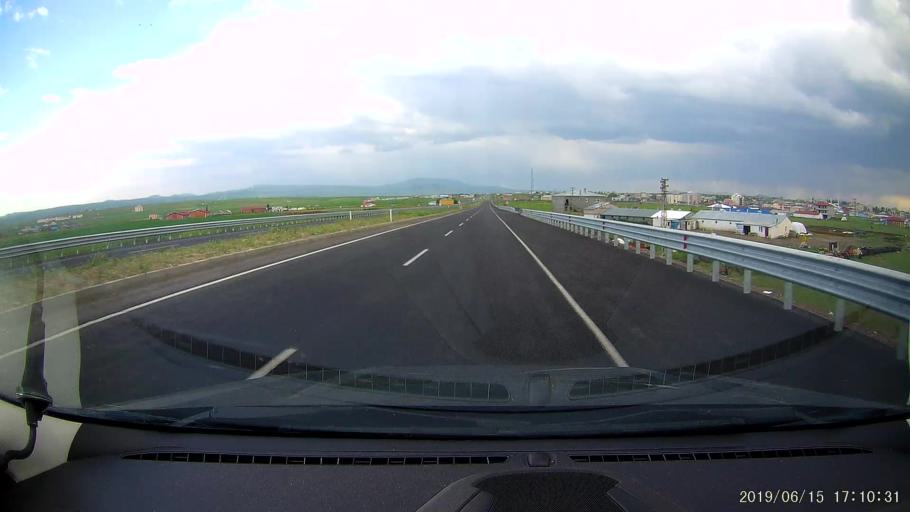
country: TR
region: Kars
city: Kars
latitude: 40.6213
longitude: 43.1337
